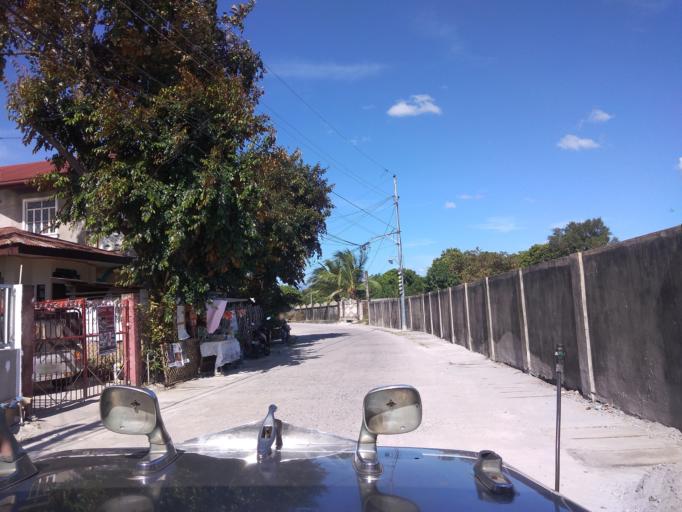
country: PH
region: Central Luzon
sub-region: Province of Pampanga
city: San Agustin
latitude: 14.9913
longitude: 120.6018
